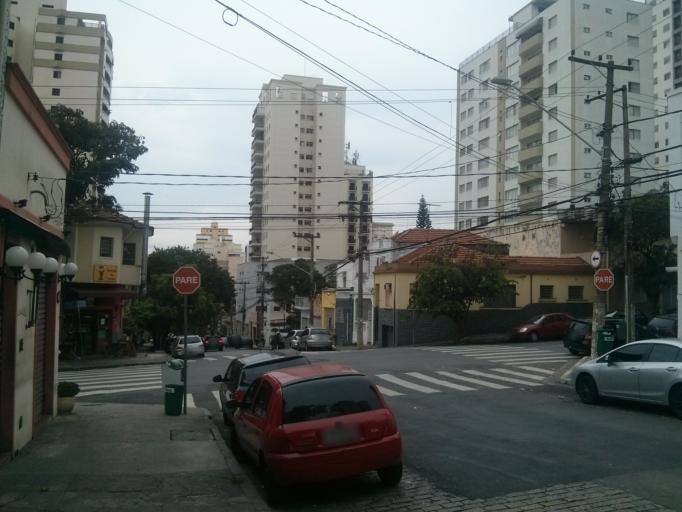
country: BR
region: Sao Paulo
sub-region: Sao Paulo
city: Sao Paulo
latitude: -23.5328
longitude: -46.6895
